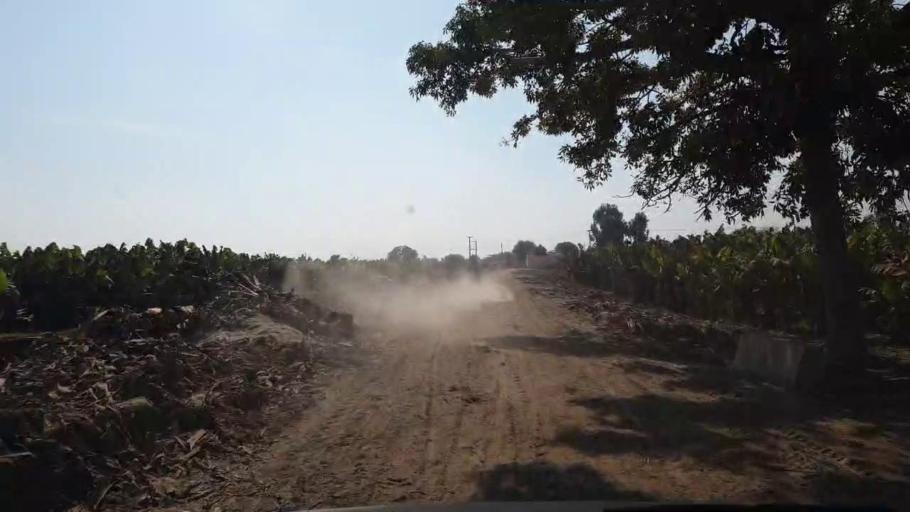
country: PK
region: Sindh
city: Chambar
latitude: 25.3713
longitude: 68.8078
